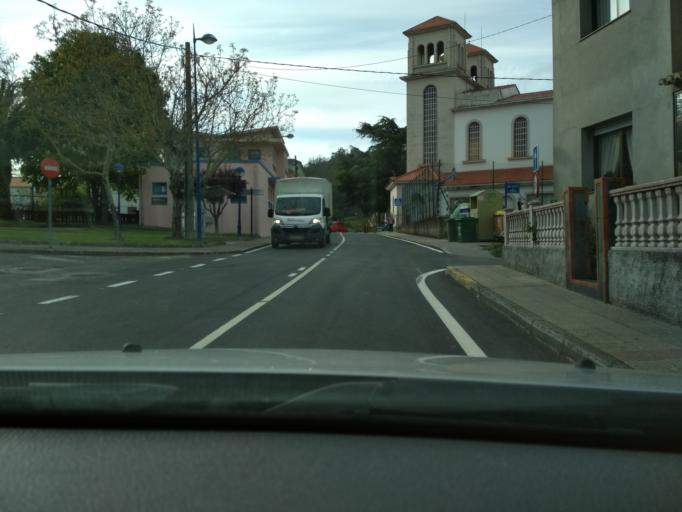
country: ES
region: Galicia
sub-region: Provincia da Coruna
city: Culleredo
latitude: 43.2875
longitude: -8.3886
